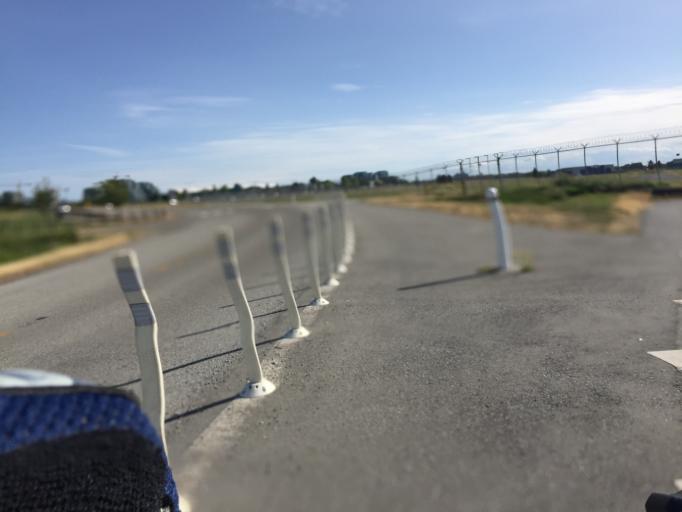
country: CA
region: British Columbia
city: Richmond
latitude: 49.1851
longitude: -123.1496
